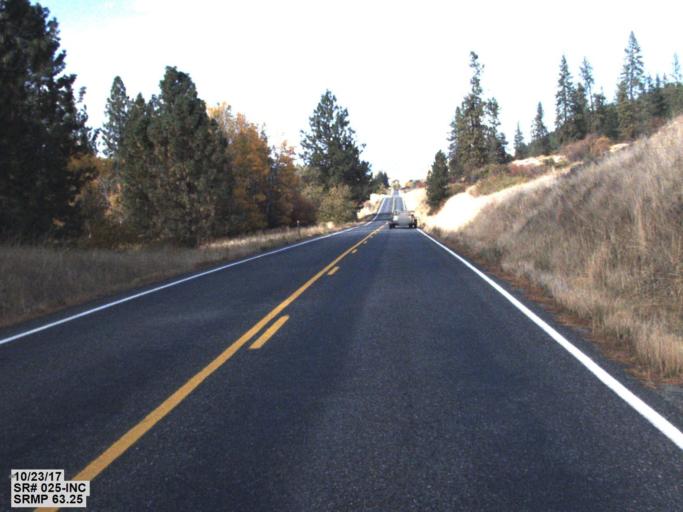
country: US
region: Washington
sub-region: Stevens County
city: Kettle Falls
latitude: 48.3847
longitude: -118.1669
